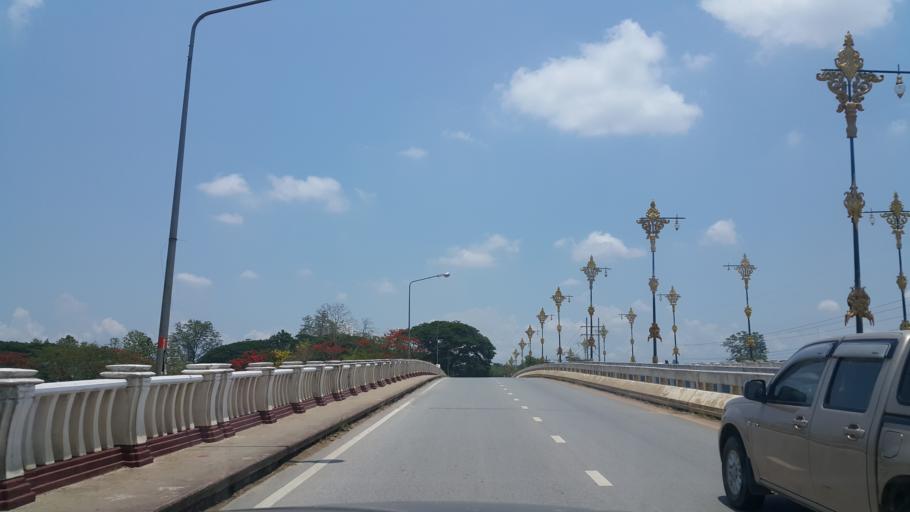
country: TH
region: Chiang Rai
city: Chiang Rai
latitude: 19.9223
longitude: 99.8177
